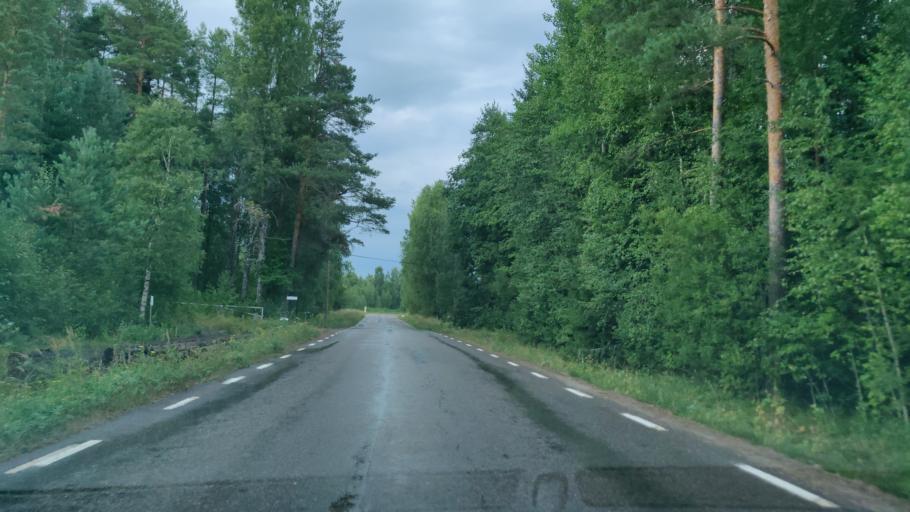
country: SE
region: Vaermland
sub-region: Munkfors Kommun
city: Munkfors
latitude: 59.8793
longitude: 13.5222
